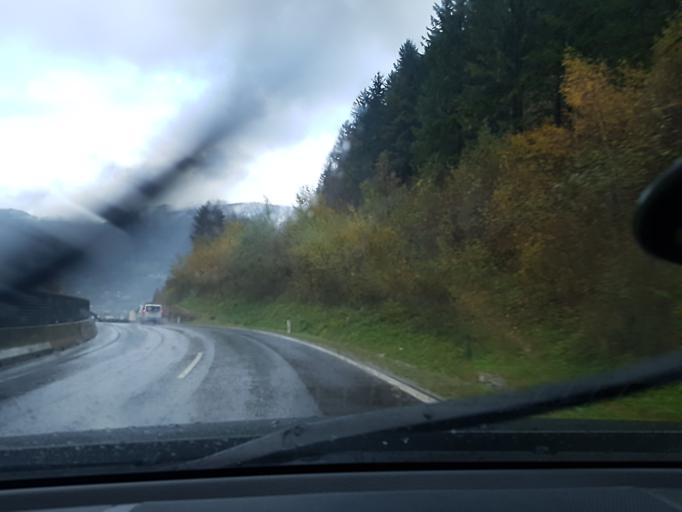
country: AT
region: Styria
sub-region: Politischer Bezirk Liezen
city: Trieben
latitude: 47.4790
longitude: 14.4857
